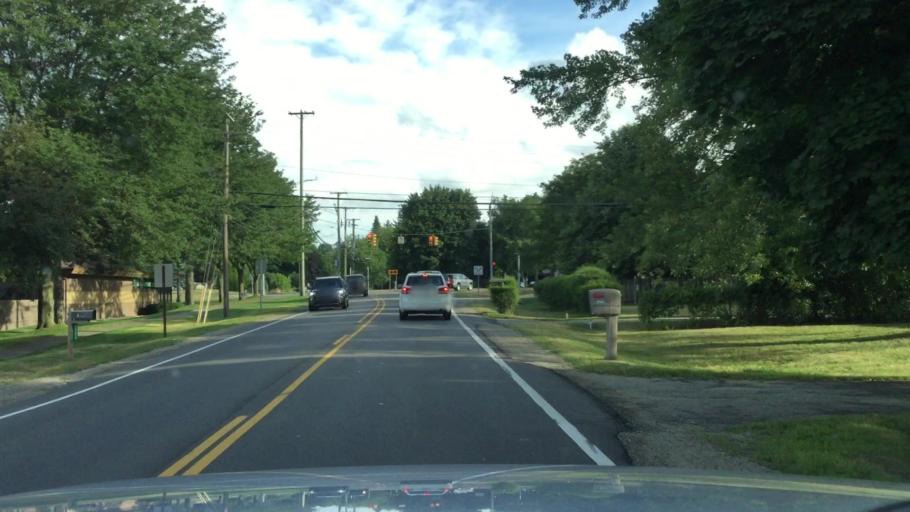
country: US
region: Michigan
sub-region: Oakland County
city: Waterford
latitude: 42.6761
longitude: -83.3813
